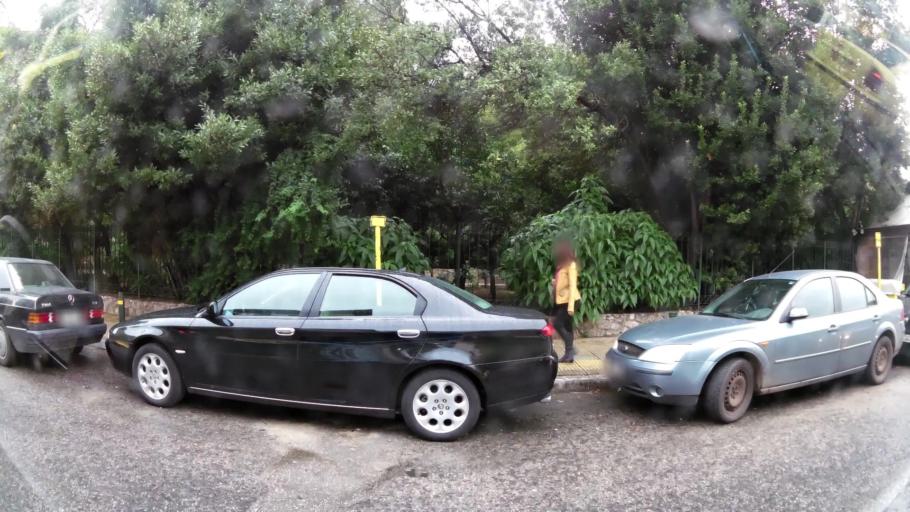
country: GR
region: Attica
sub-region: Nomarchia Athinas
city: Vyronas
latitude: 37.9701
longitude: 23.7473
